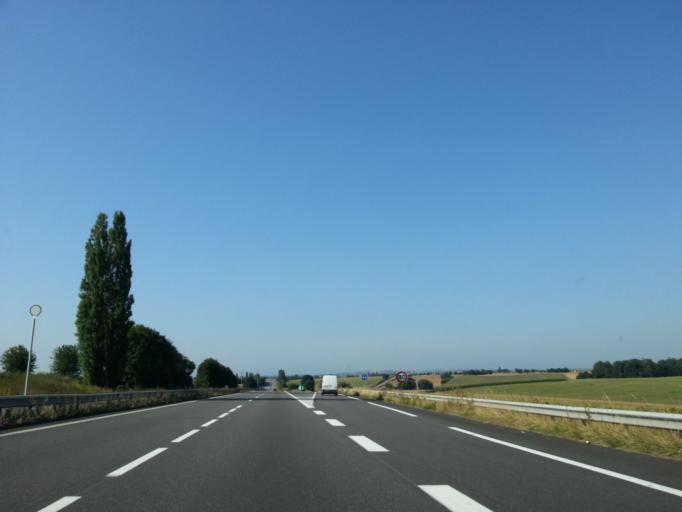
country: FR
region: Alsace
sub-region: Departement du Bas-Rhin
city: Niederschaeffolsheim
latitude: 48.7718
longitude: 7.7123
